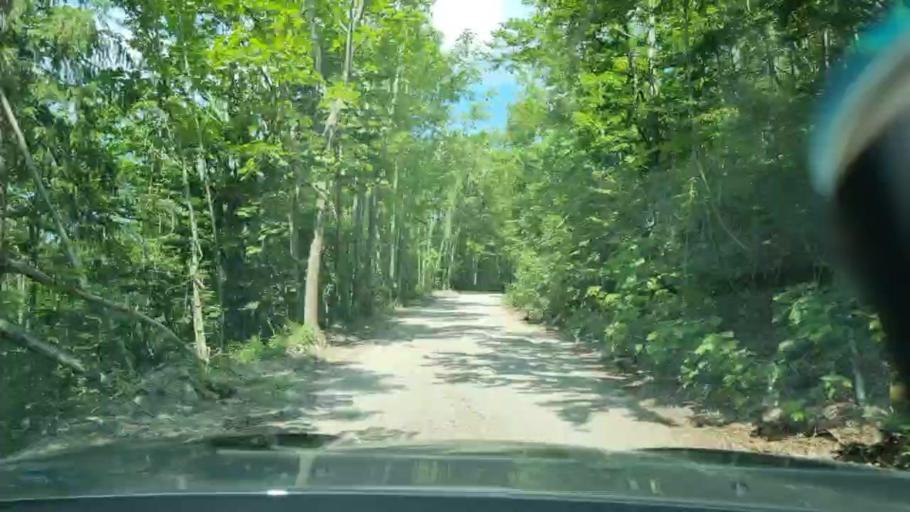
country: BA
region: Federation of Bosnia and Herzegovina
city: Bosansko Grahovo
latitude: 44.3261
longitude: 16.2395
